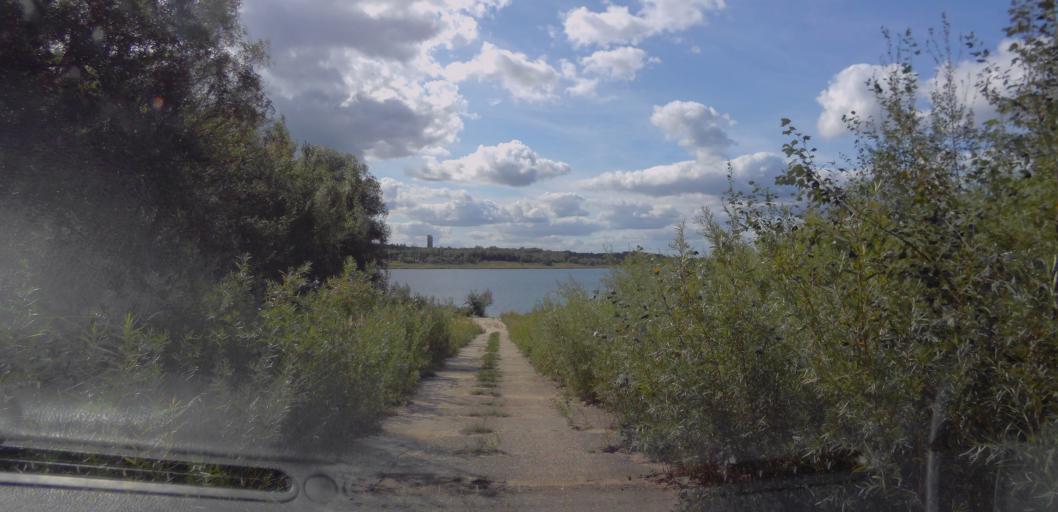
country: PL
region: Subcarpathian Voivodeship
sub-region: Tarnobrzeg
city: Tarnobrzeg
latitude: 50.5345
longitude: 21.6537
